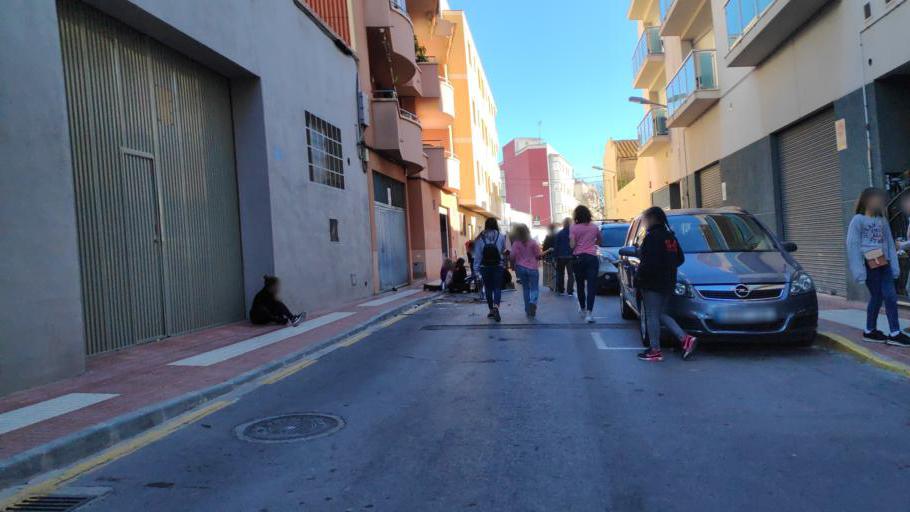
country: ES
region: Valencia
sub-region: Provincia de Castello
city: Benicassim
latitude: 40.0554
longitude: 0.0615
